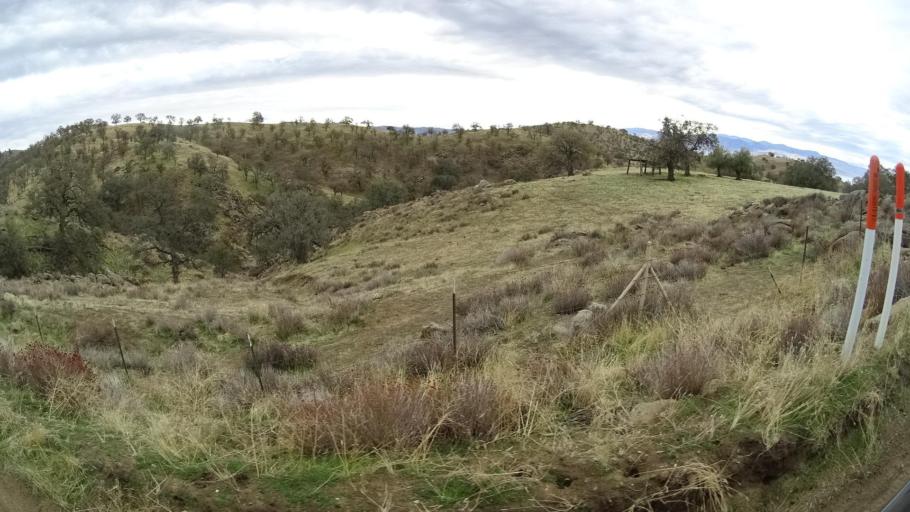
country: US
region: California
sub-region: Kern County
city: Stallion Springs
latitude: 35.1237
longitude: -118.7377
